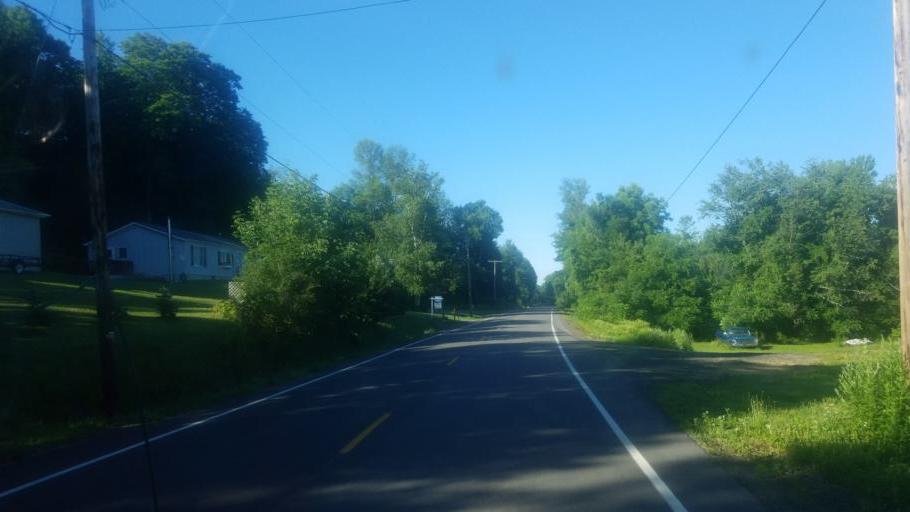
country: US
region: New York
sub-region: Wayne County
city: Newark
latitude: 43.0820
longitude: -77.0702
